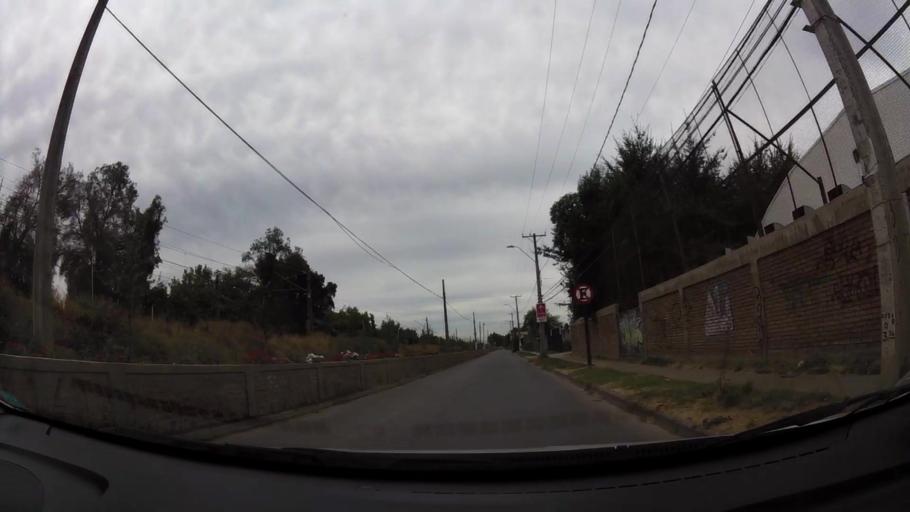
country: CL
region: O'Higgins
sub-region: Provincia de Cachapoal
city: Graneros
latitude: -34.0730
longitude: -70.7273
